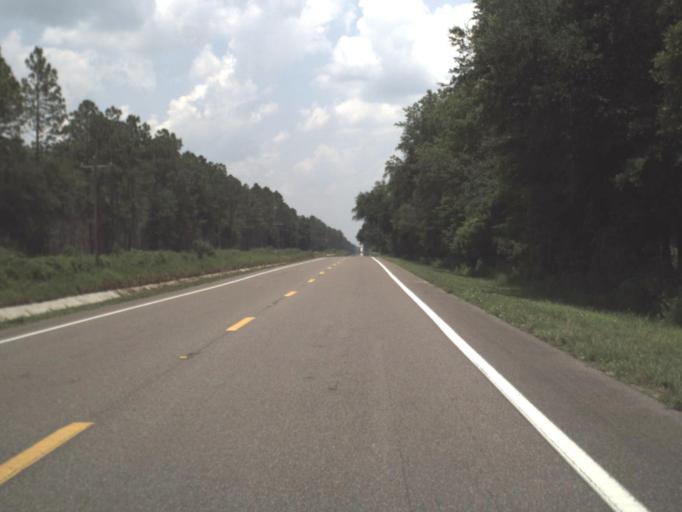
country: US
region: Florida
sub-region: Putnam County
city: Palatka
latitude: 29.4972
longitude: -81.7456
